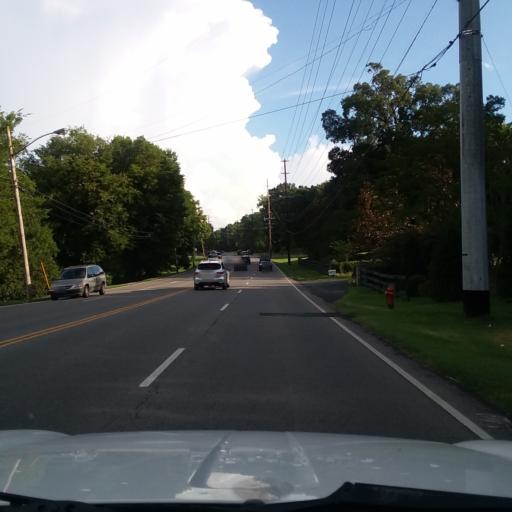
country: US
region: Tennessee
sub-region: Davidson County
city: Oak Hill
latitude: 36.0737
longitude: -86.7739
